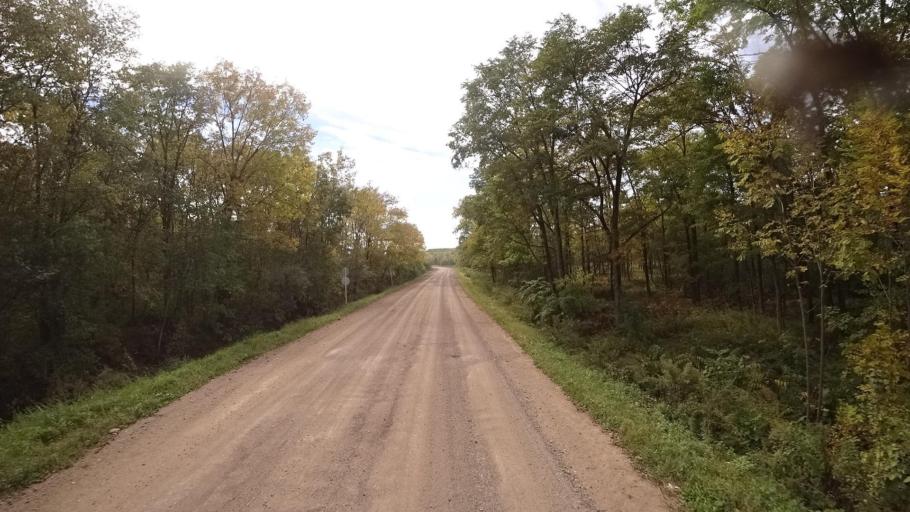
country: RU
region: Primorskiy
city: Yakovlevka
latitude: 44.5319
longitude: 133.6010
